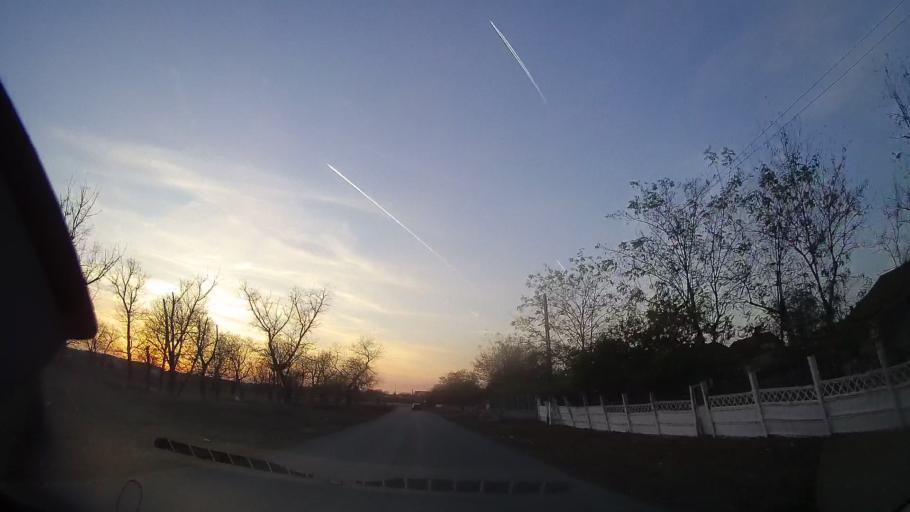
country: RO
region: Constanta
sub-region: Comuna Mereni
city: Mereni
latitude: 44.0163
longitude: 28.3232
